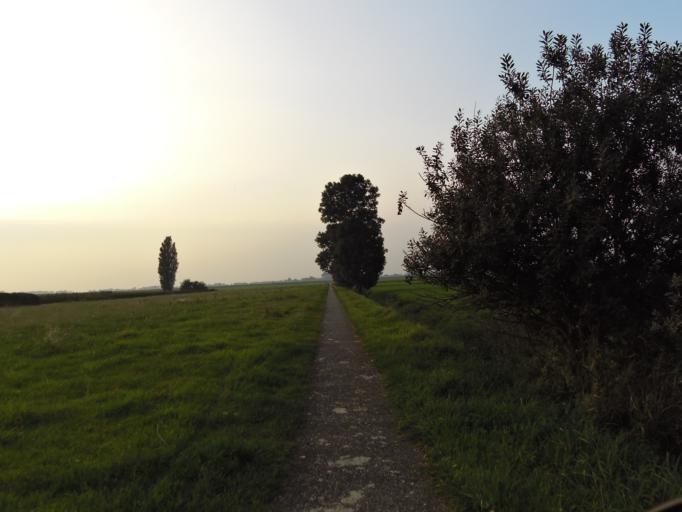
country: NL
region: South Holland
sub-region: Gemeente Rijnwoude
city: Benthuizen
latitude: 52.0945
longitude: 4.5332
